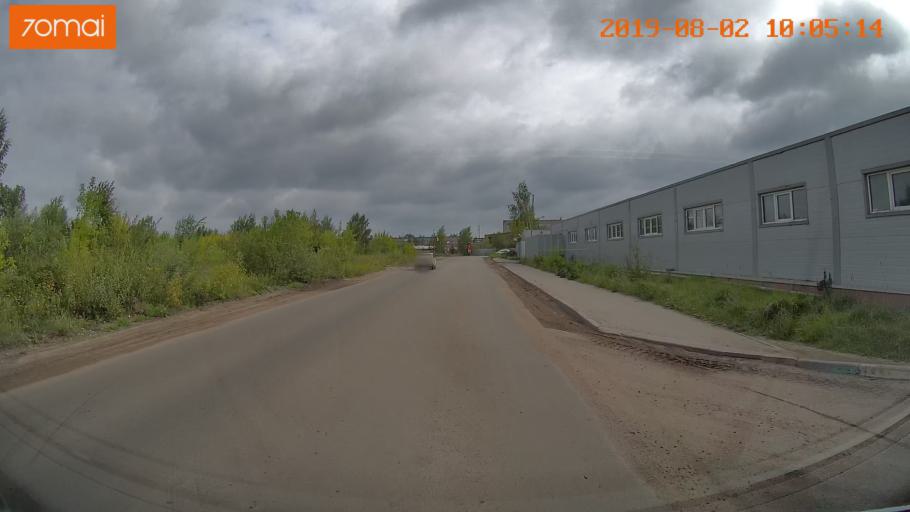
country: RU
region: Ivanovo
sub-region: Gorod Ivanovo
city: Ivanovo
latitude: 56.9774
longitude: 40.9244
